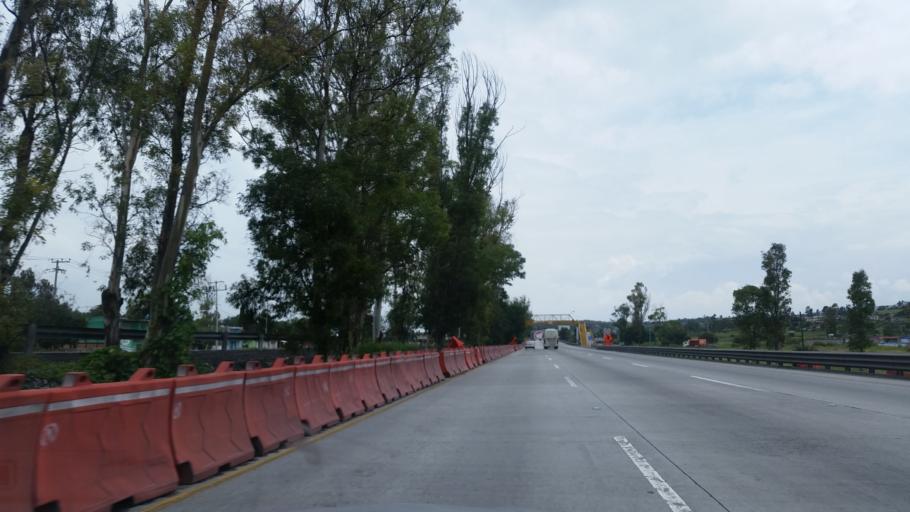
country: MX
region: Mexico
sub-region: Huehuetoca
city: Villa URBI del Rey
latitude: 19.8407
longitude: -99.2771
